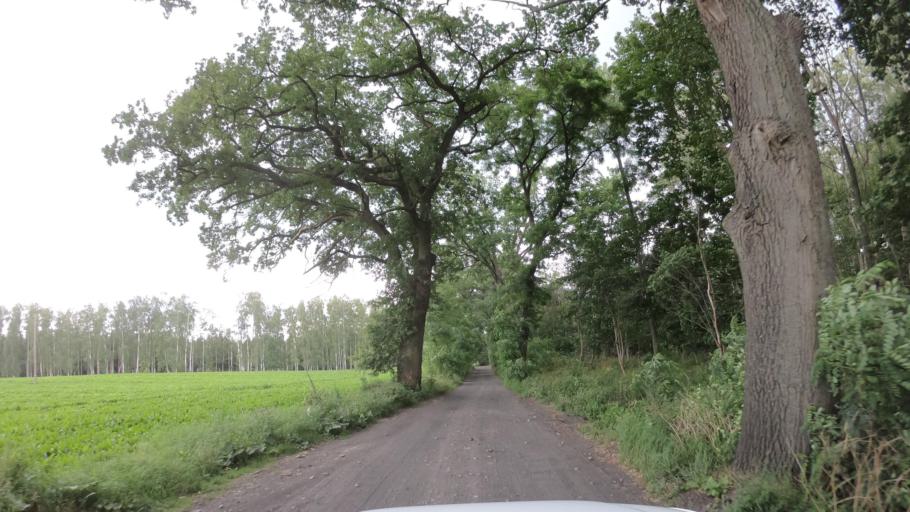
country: PL
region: West Pomeranian Voivodeship
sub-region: Powiat stargardzki
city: Dolice
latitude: 53.1947
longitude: 15.2822
